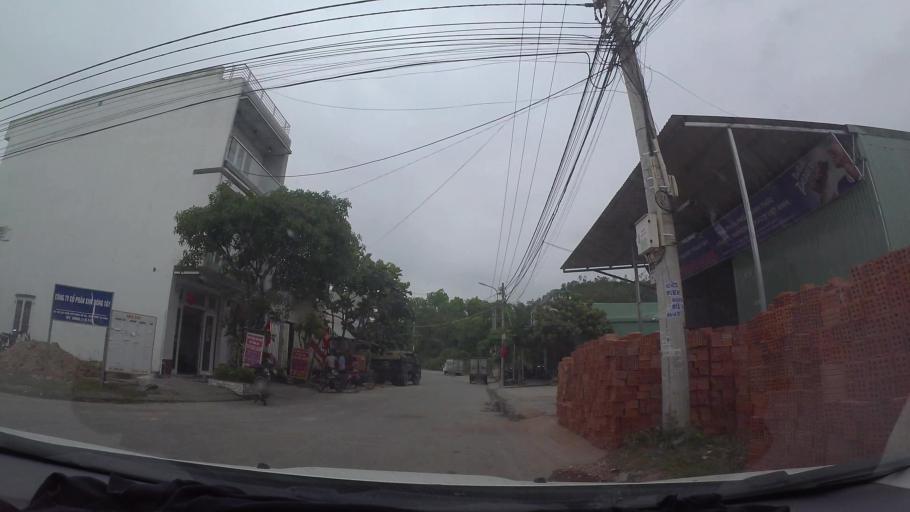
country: VN
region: Da Nang
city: Lien Chieu
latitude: 16.0665
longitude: 108.1443
